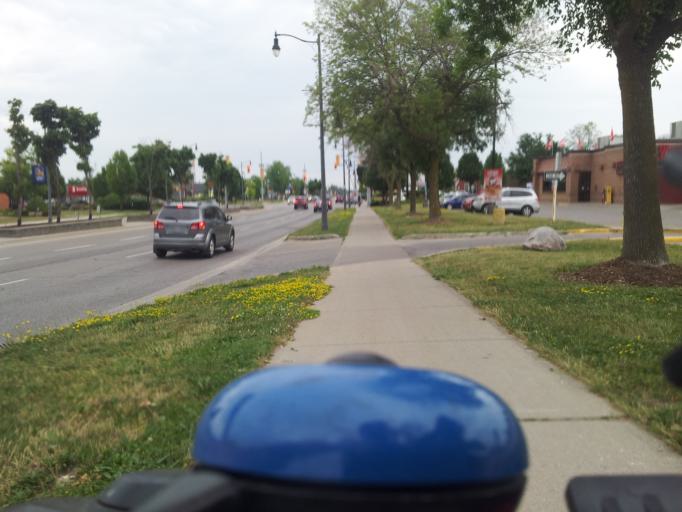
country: CA
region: Ontario
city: Stratford
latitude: 43.3707
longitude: -80.9496
